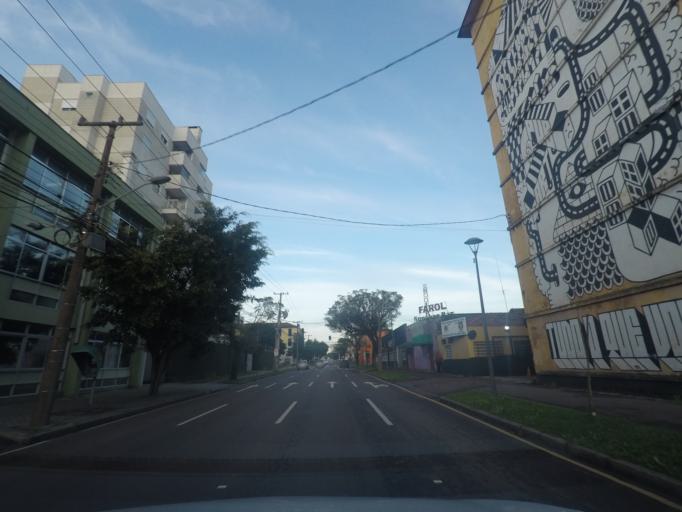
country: BR
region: Parana
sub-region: Curitiba
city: Curitiba
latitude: -25.4429
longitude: -49.2623
